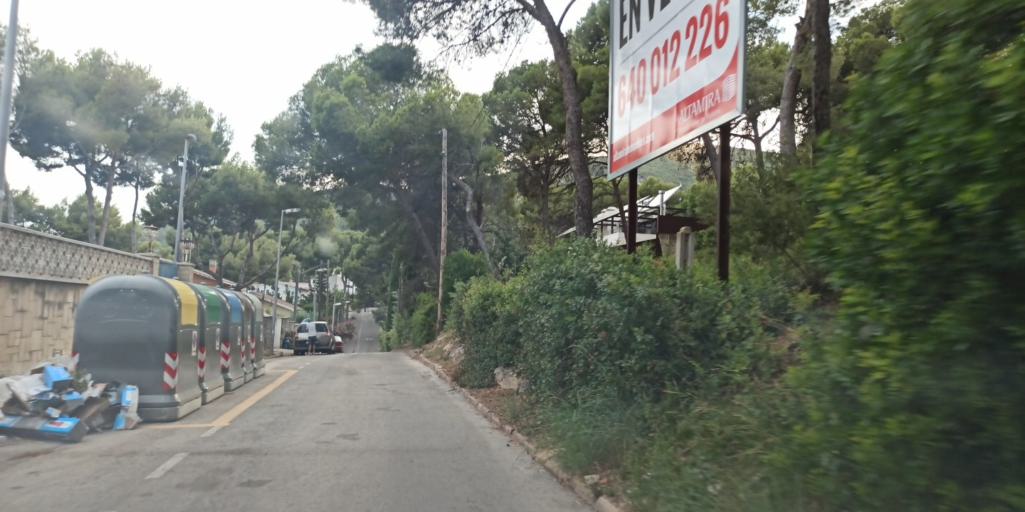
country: ES
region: Catalonia
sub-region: Provincia de Barcelona
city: Castelldefels
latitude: 41.2821
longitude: 1.9640
